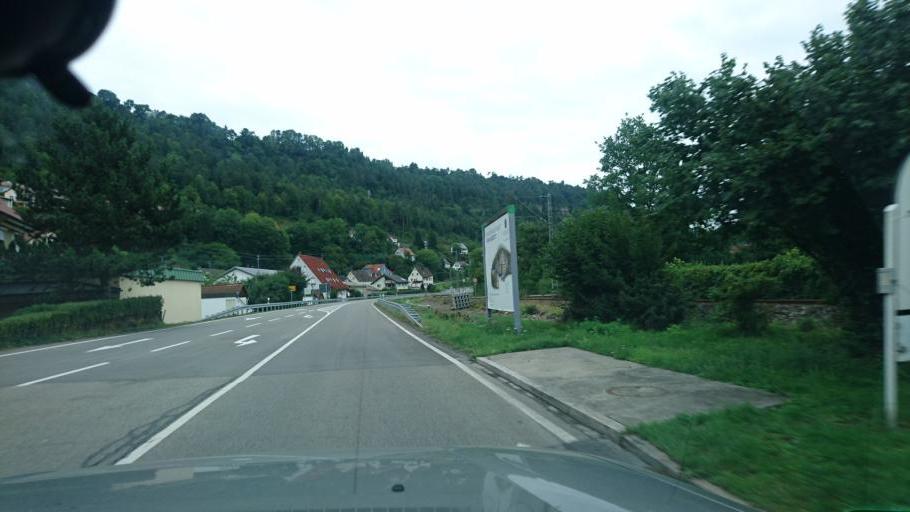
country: DE
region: Baden-Wuerttemberg
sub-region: Freiburg Region
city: Oberndorf
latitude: 48.3164
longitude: 8.5707
